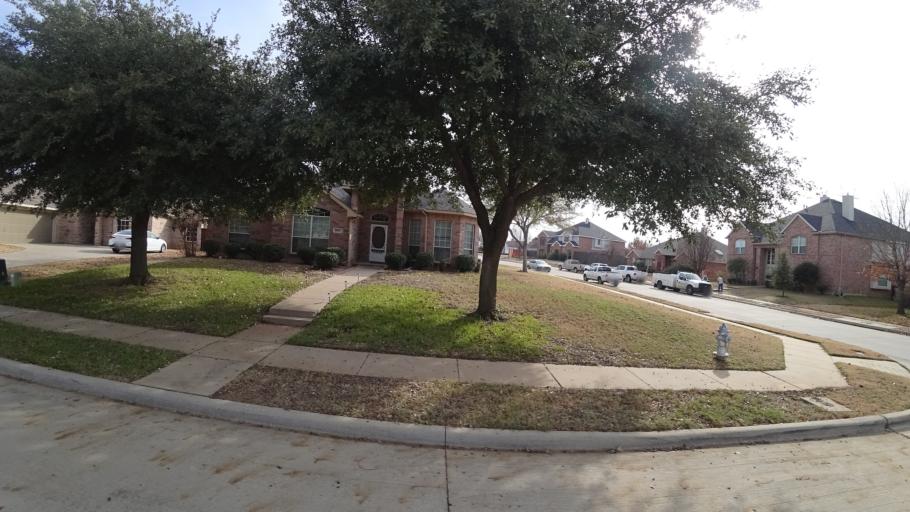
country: US
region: Texas
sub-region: Denton County
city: Highland Village
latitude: 33.0751
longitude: -97.0367
